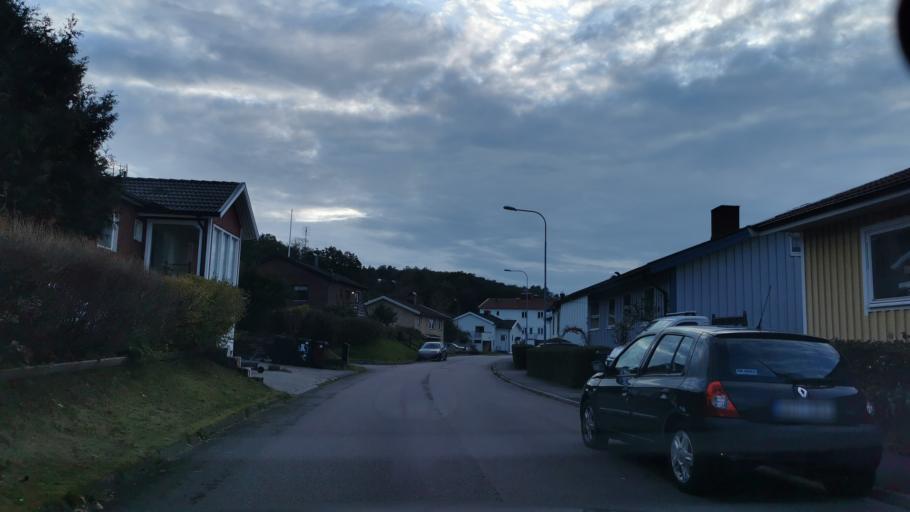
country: SE
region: Vaestra Goetaland
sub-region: Partille Kommun
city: Partille
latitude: 57.7234
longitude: 12.0915
